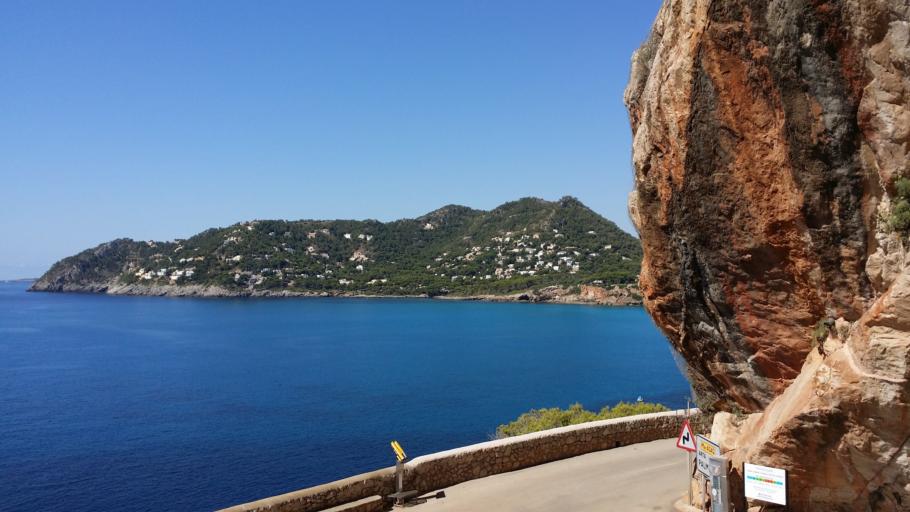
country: ES
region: Balearic Islands
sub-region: Illes Balears
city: Capdepera
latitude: 39.6560
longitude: 3.4504
